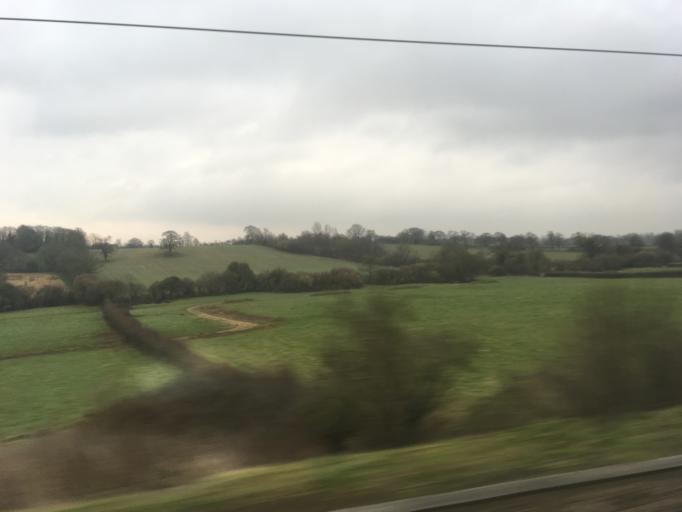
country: GB
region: England
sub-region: Wiltshire
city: Malmesbury
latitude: 51.5439
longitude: -2.1019
